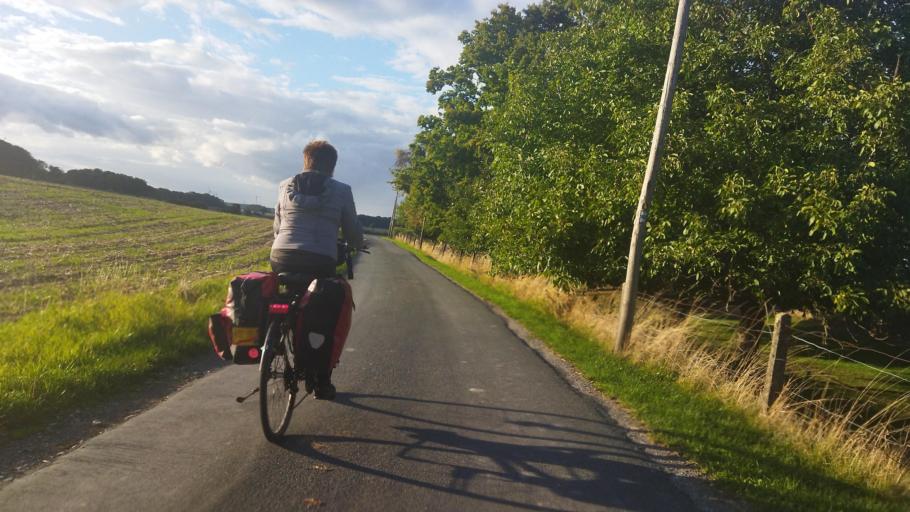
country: DE
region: North Rhine-Westphalia
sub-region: Regierungsbezirk Munster
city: Billerbeck
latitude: 51.9586
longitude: 7.2597
